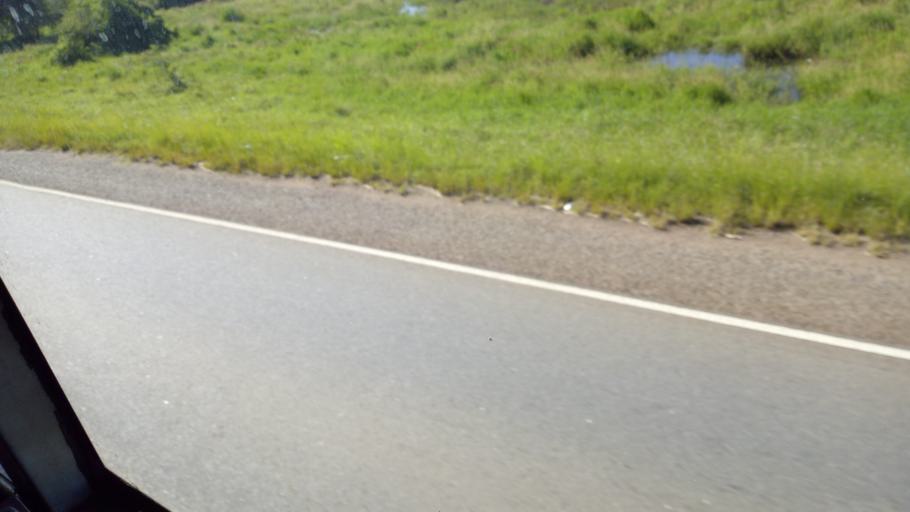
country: UG
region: Central Region
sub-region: Lyantonde District
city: Lyantonde
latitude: -0.4533
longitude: 31.0543
